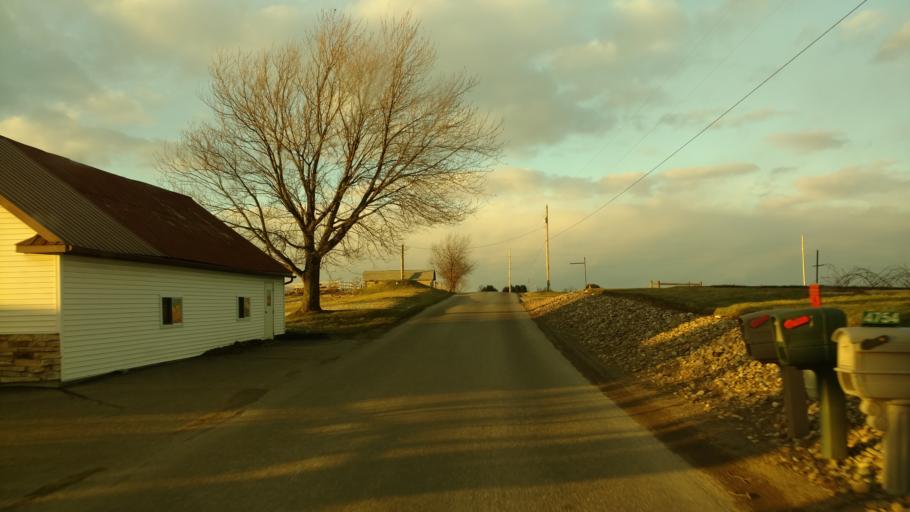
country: US
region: Ohio
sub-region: Holmes County
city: Millersburg
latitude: 40.5395
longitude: -81.7780
